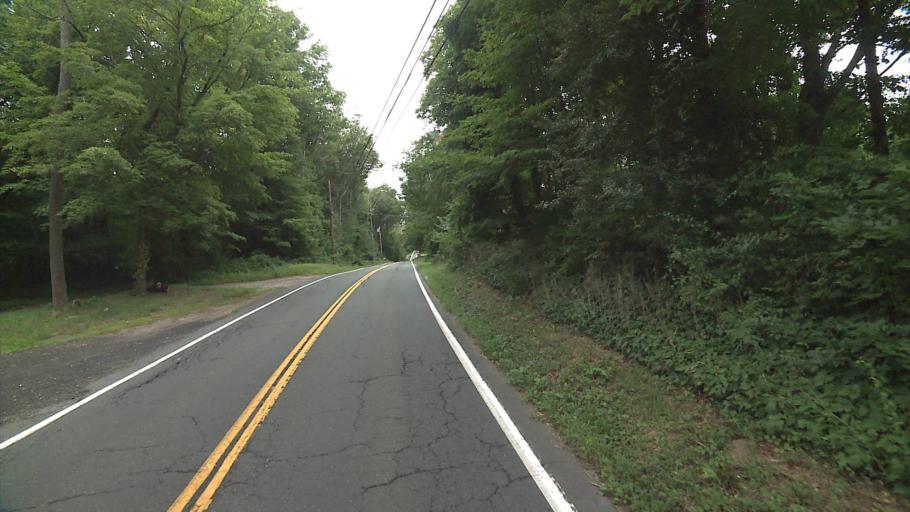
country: US
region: Connecticut
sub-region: Hartford County
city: Manchester
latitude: 41.7952
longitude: -72.4730
